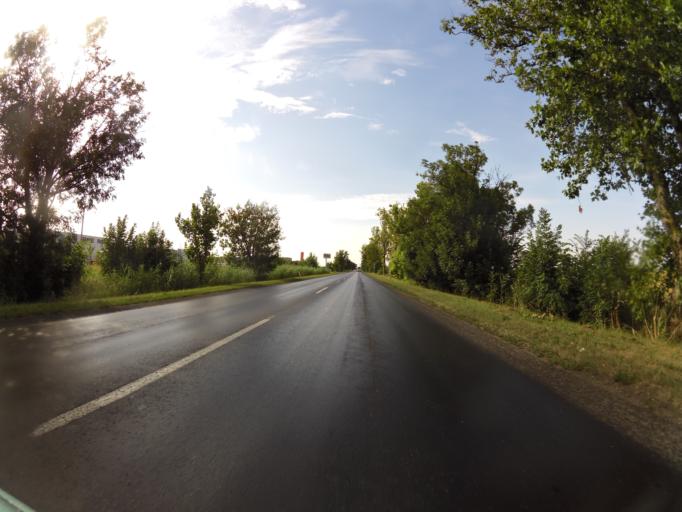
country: HU
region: Csongrad
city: Szeged
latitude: 46.2851
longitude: 20.0899
